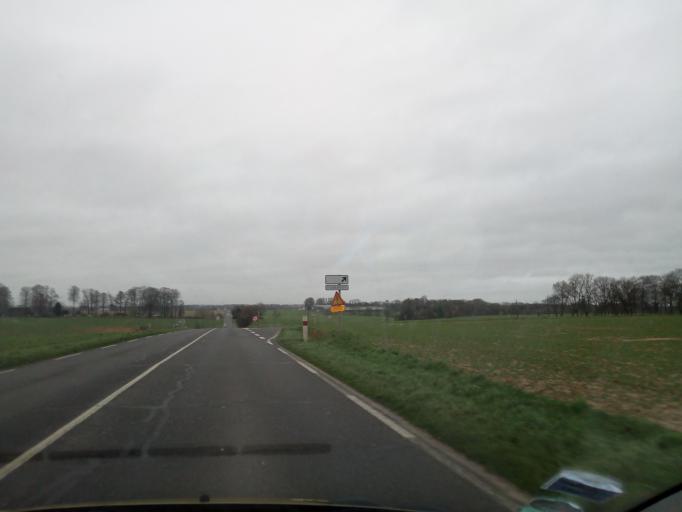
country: FR
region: Haute-Normandie
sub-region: Departement de la Seine-Maritime
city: Auzebosc
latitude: 49.5889
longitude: 0.7337
